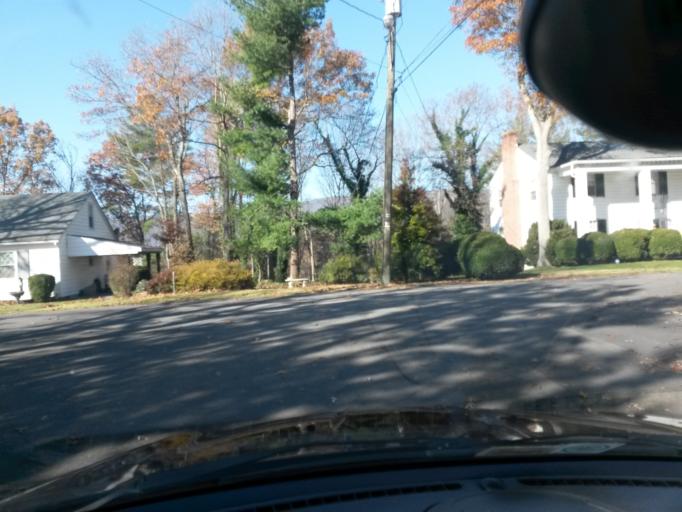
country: US
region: Virginia
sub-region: Alleghany County
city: Clifton Forge
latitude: 37.8269
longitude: -79.8242
